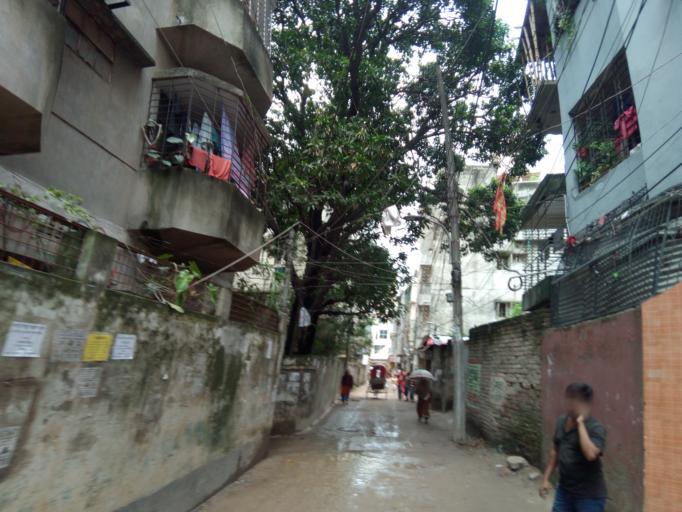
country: BD
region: Dhaka
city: Azimpur
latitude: 23.7435
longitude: 90.3654
